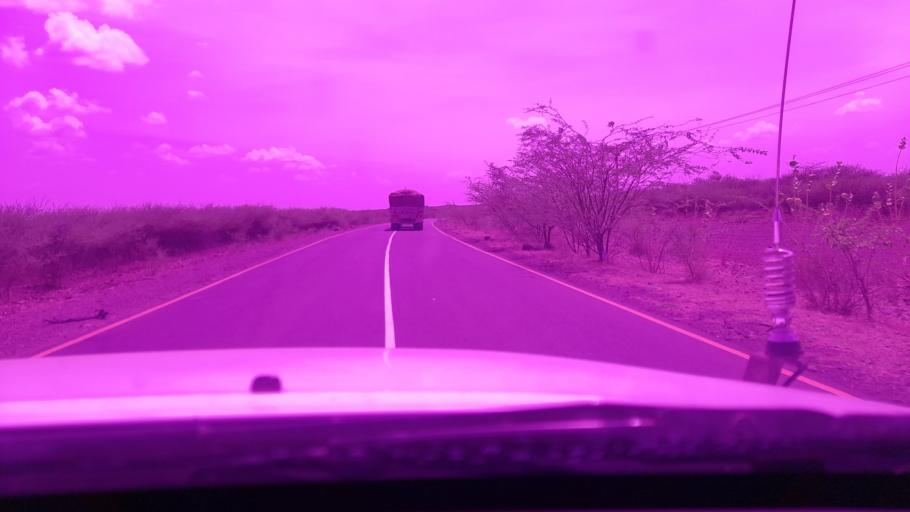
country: ET
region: Afar
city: Awash
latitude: 9.3502
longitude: 40.2972
